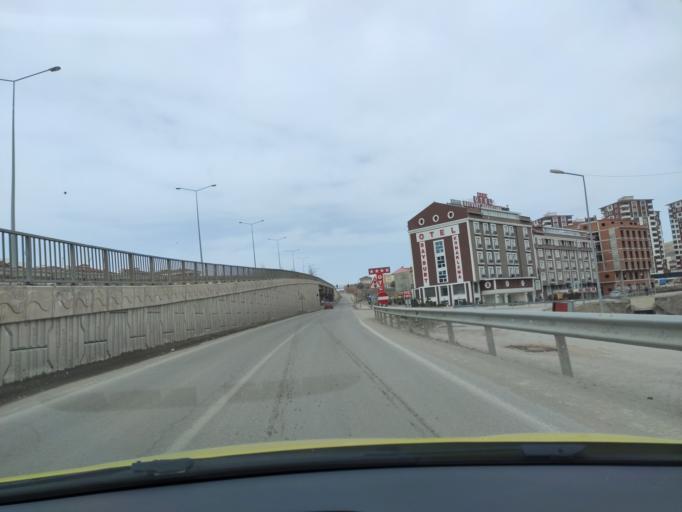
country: TR
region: Bayburt
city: Bayburt
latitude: 40.2582
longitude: 40.2143
